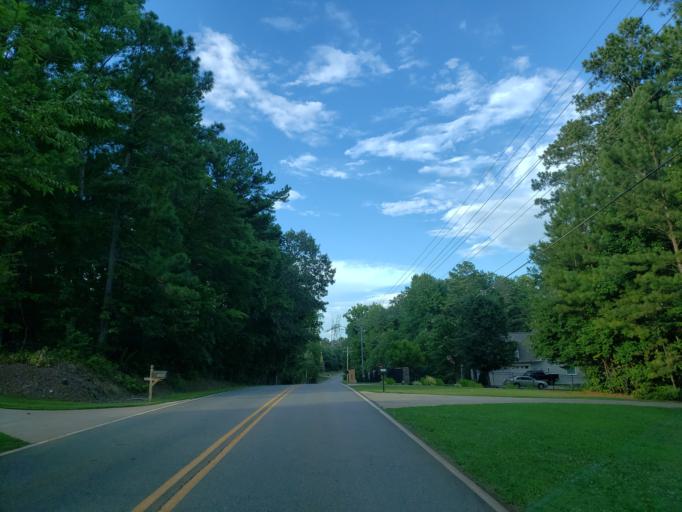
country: US
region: Georgia
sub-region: Cherokee County
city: Canton
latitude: 34.3235
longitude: -84.5173
